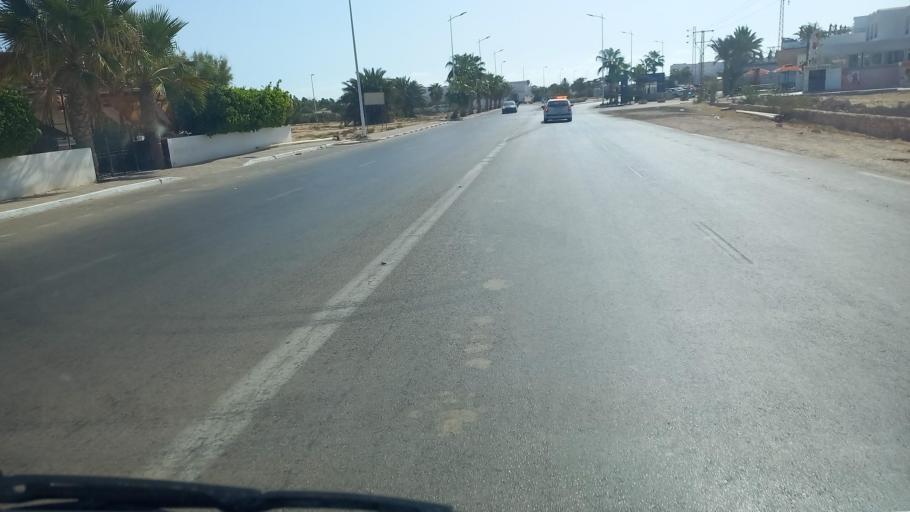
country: TN
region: Madanin
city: Midoun
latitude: 33.8368
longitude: 10.9990
